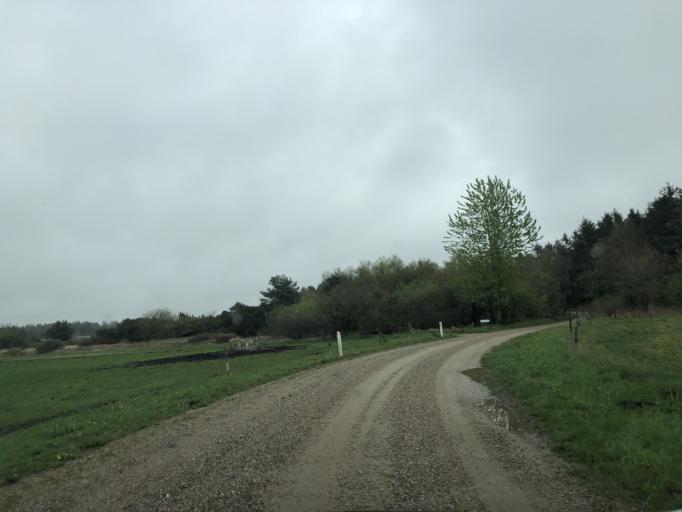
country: DK
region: Central Jutland
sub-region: Lemvig Kommune
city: Lemvig
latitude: 56.4442
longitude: 8.3811
